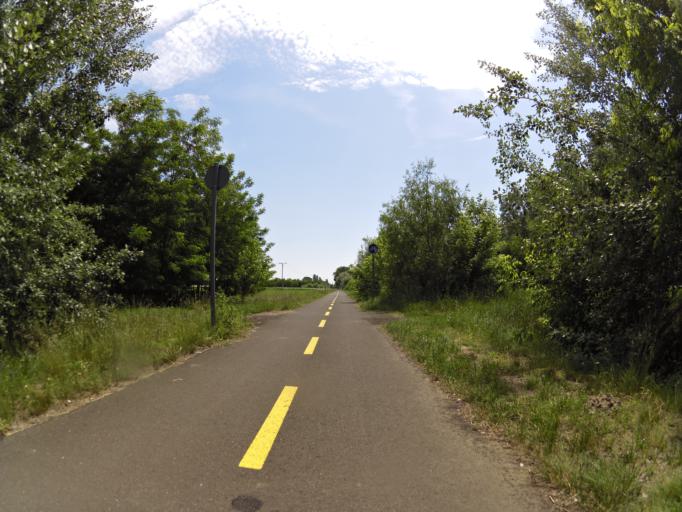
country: HU
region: Csongrad
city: Kistelek
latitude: 46.4522
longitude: 19.9958
